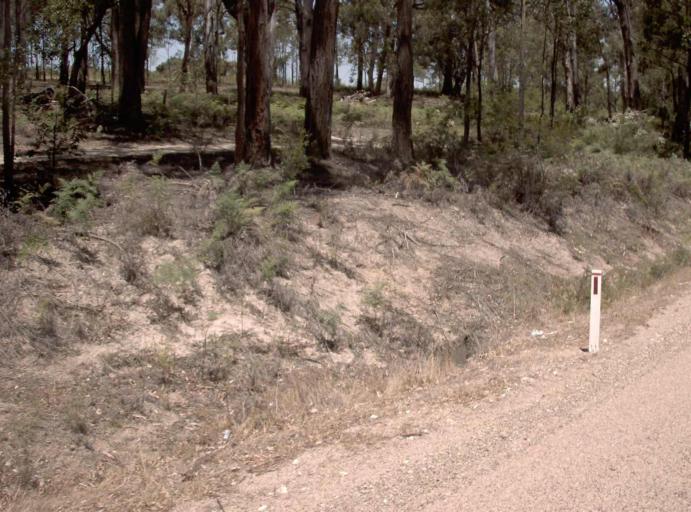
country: AU
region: Victoria
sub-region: East Gippsland
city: Bairnsdale
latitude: -37.7407
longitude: 147.7654
